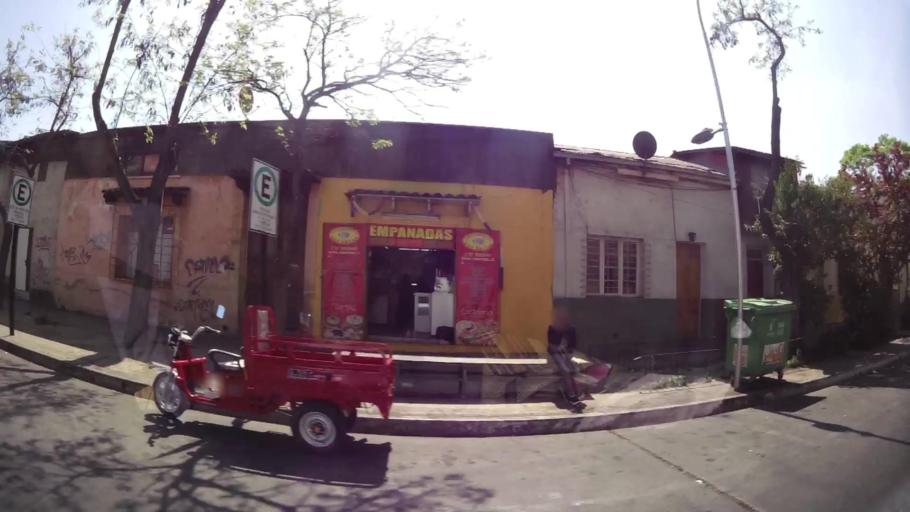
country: CL
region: Santiago Metropolitan
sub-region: Provincia de Santiago
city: Santiago
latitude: -33.4529
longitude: -70.6656
